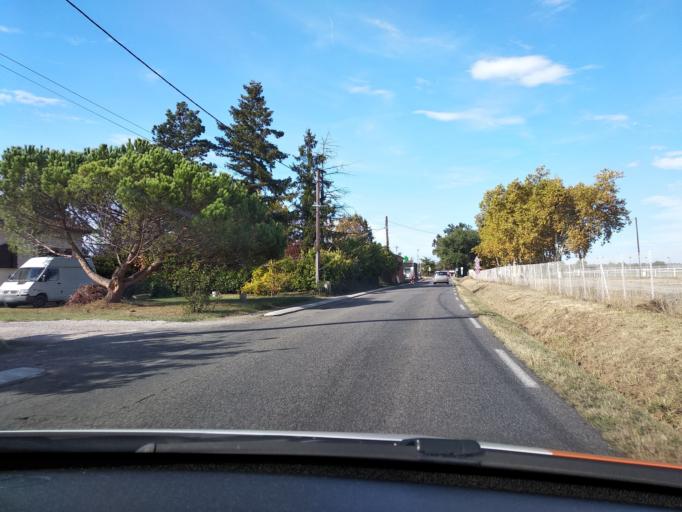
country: FR
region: Midi-Pyrenees
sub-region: Departement du Tarn-et-Garonne
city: Montauban
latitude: 44.0370
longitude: 1.3396
